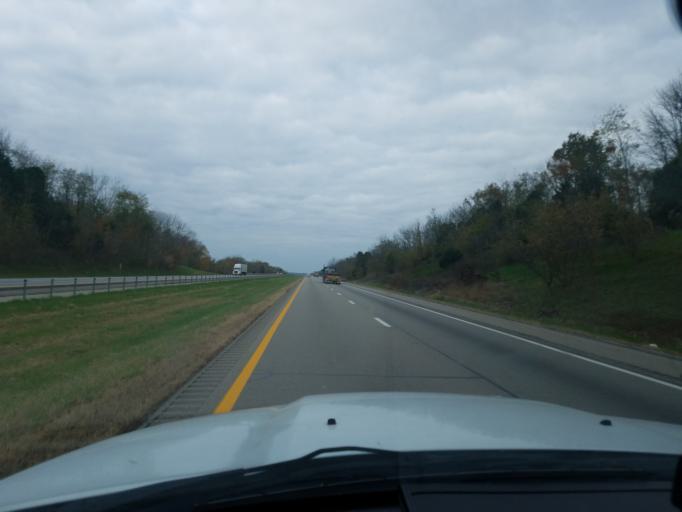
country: US
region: Kentucky
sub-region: Carroll County
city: Carrollton
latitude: 38.6524
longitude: -85.0916
